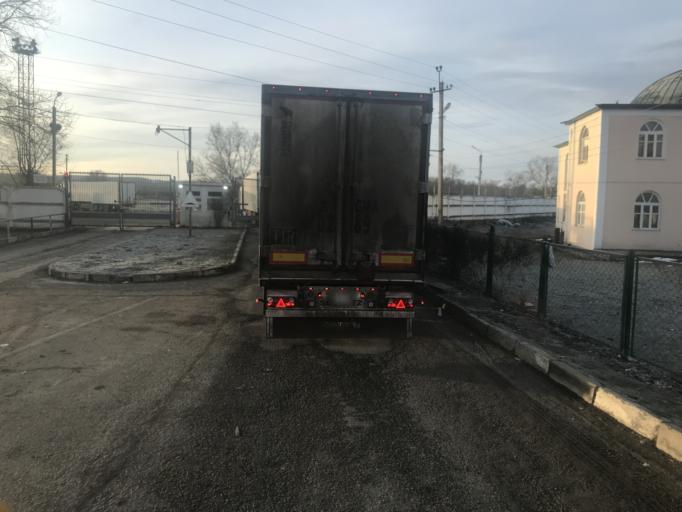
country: AZ
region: Qusar
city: Samur
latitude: 41.6420
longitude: 48.4050
